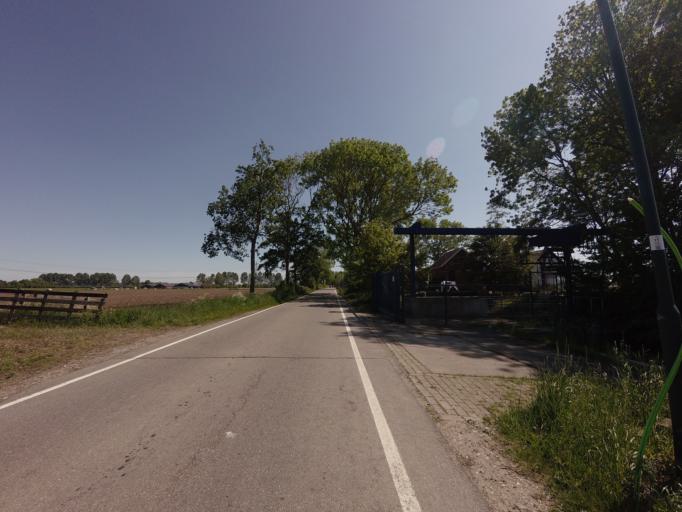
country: NL
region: Utrecht
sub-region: Gemeente Woerden
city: Woerden
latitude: 52.1090
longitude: 4.9379
